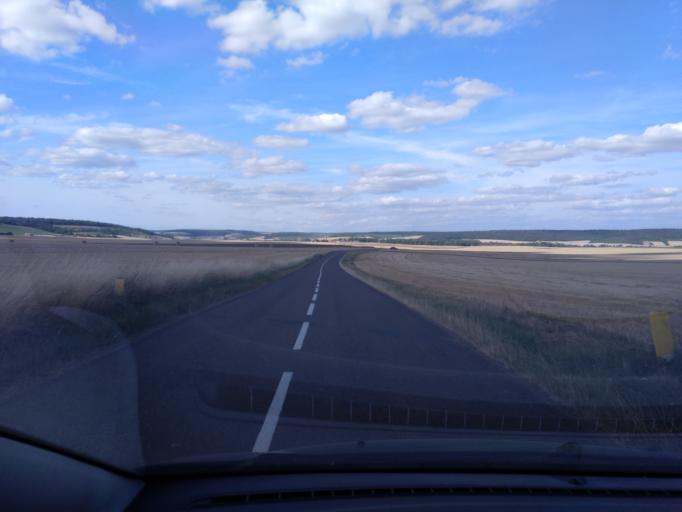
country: FR
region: Bourgogne
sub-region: Departement de la Cote-d'Or
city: Chatillon-sur-Seine
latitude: 47.9227
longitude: 4.6353
